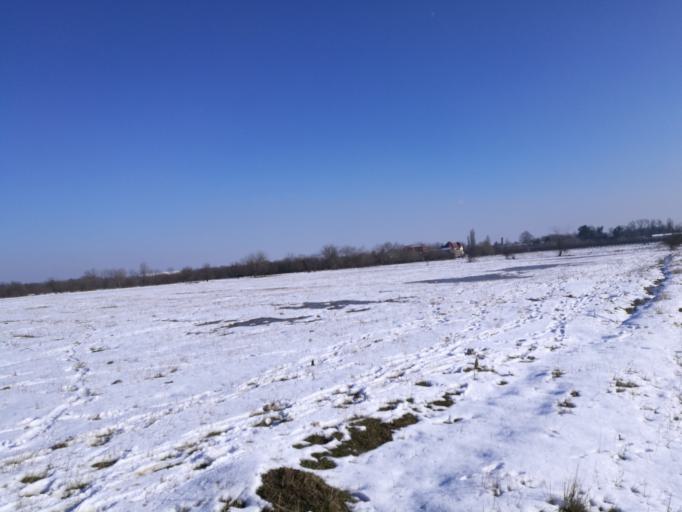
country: RO
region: Ilfov
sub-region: Comuna Otopeni
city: Otopeni
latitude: 44.5032
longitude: 26.0640
